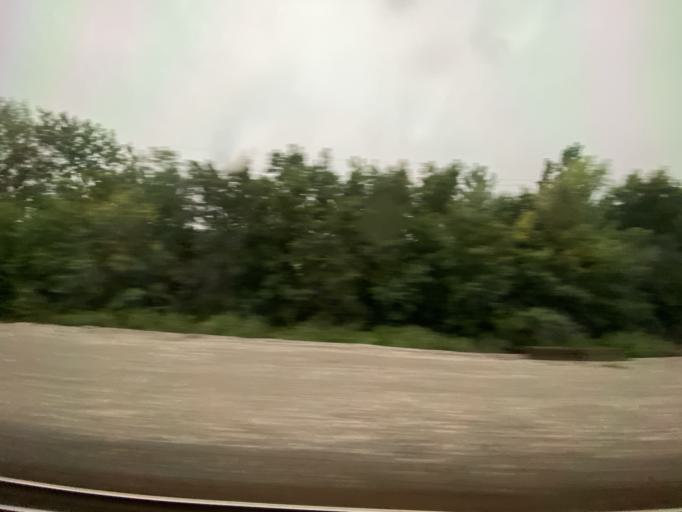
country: US
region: Iowa
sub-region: Lee County
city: Fort Madison
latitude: 40.6191
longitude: -91.2805
